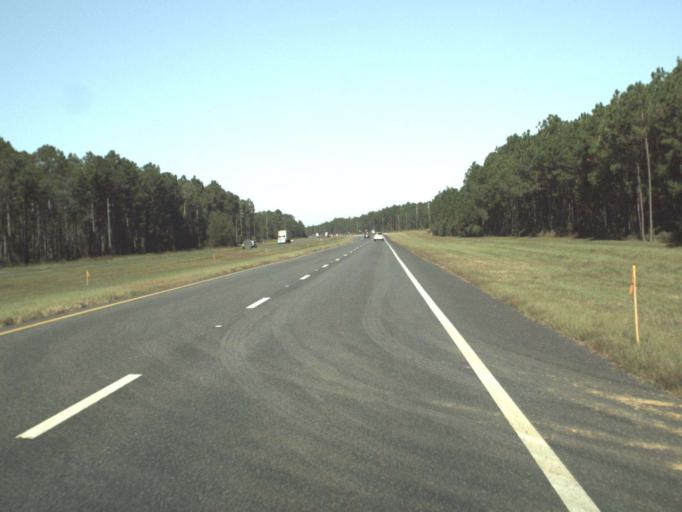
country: US
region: Florida
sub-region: Walton County
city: Seaside
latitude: 30.3453
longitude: -86.0750
